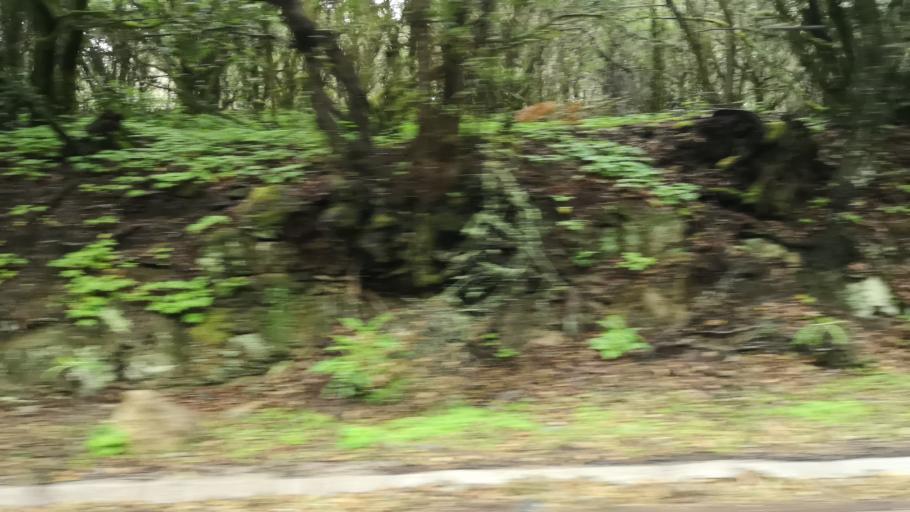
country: ES
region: Canary Islands
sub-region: Provincia de Santa Cruz de Tenerife
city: Vallehermosa
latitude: 28.1275
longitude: -17.2579
